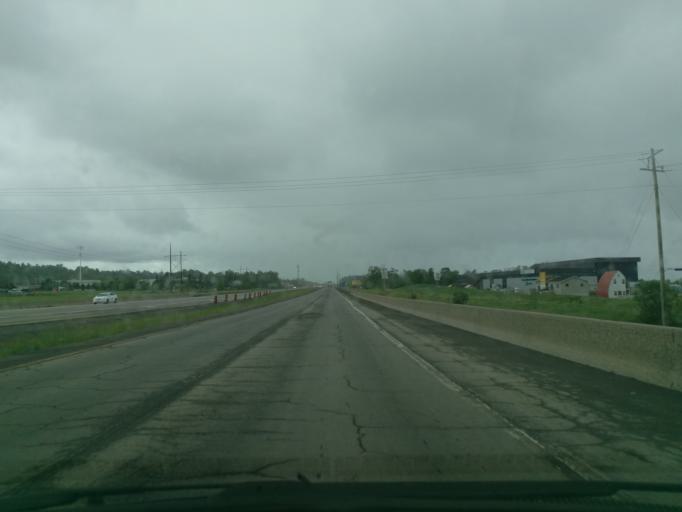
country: CA
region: Ontario
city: Clarence-Rockland
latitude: 45.4950
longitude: -75.4830
